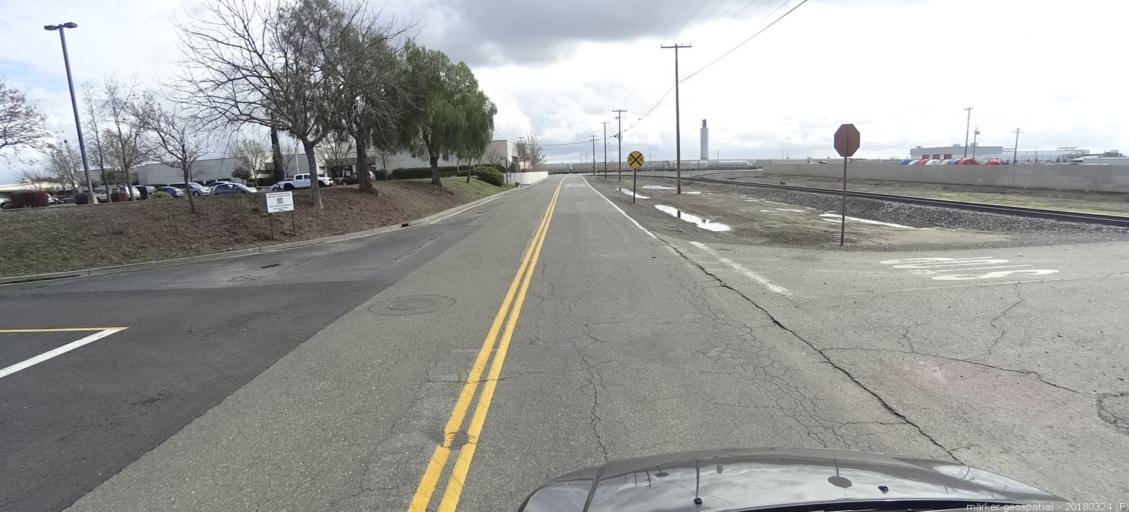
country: US
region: California
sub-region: Sacramento County
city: North Highlands
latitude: 38.6508
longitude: -121.4084
